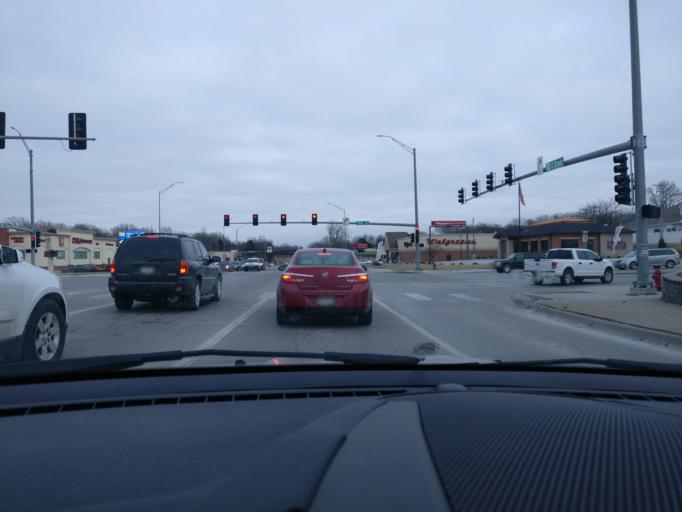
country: US
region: Nebraska
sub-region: Lancaster County
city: Lincoln
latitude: 40.8133
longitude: -96.6256
